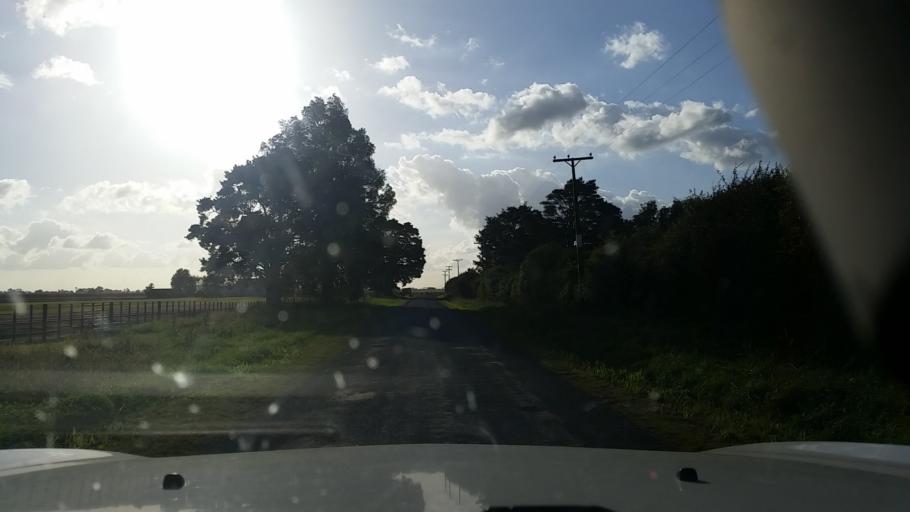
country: NZ
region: Waikato
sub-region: Matamata-Piako District
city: Matamata
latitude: -37.7398
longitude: 175.7562
